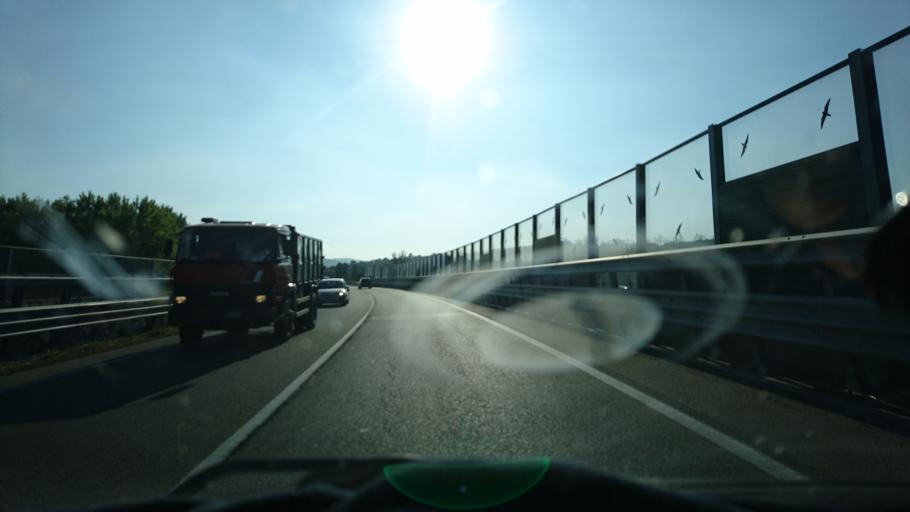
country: IT
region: Piedmont
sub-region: Provincia di Alessandria
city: Strevi
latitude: 44.6971
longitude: 8.5310
